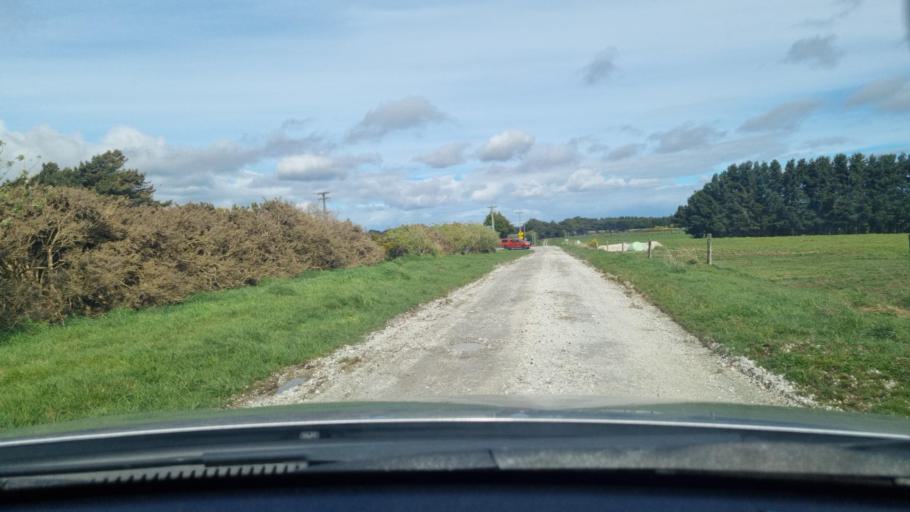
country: NZ
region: Southland
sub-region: Invercargill City
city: Invercargill
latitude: -46.4574
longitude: 168.3873
